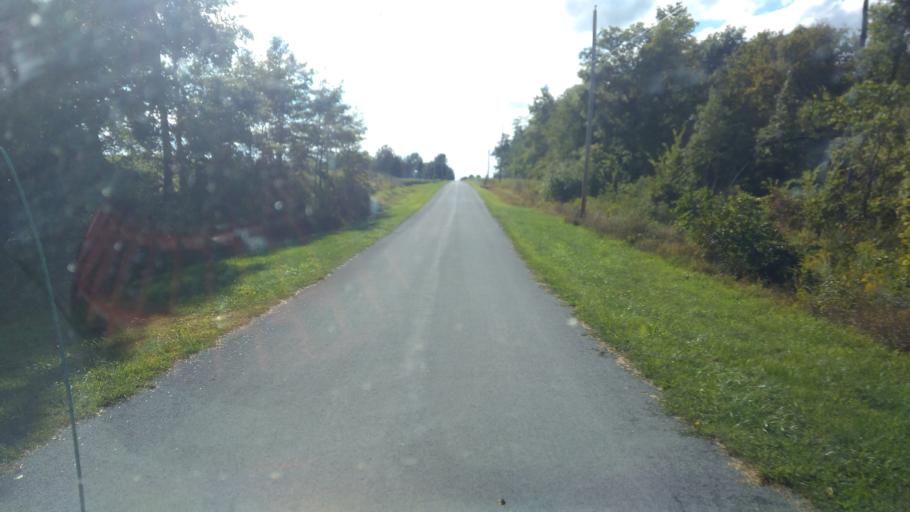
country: US
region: Ohio
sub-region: Hardin County
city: Kenton
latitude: 40.7175
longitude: -83.6559
